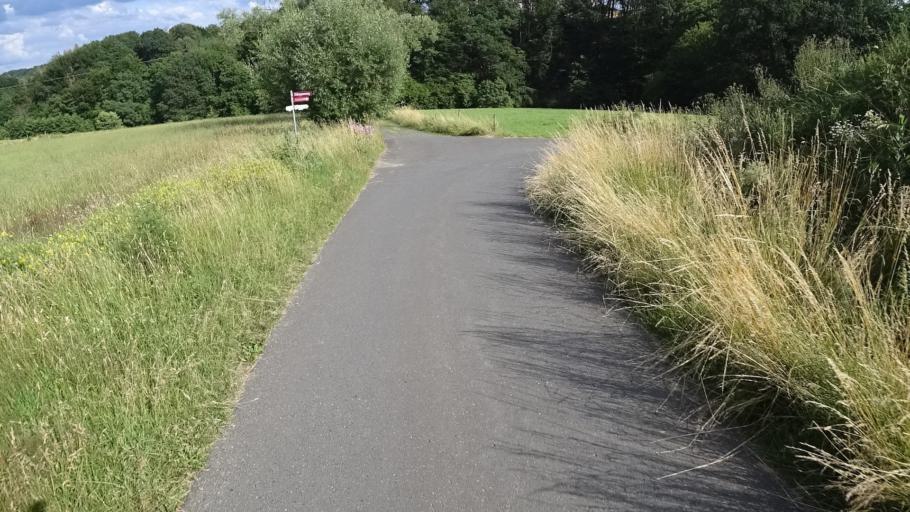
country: DE
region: Rheinland-Pfalz
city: Vettelschoss
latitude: 50.6149
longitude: 7.3475
